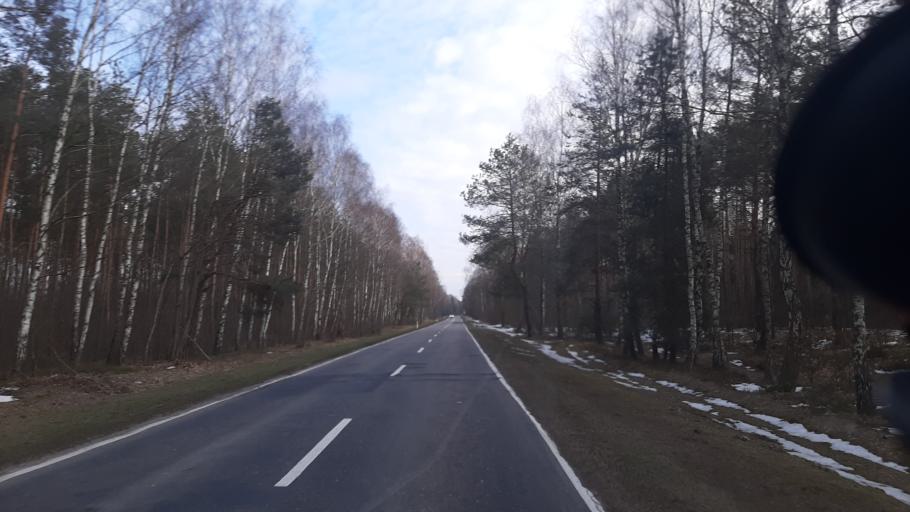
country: PL
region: Lublin Voivodeship
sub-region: Powiat lubartowski
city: Ostrow Lubelski
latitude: 51.4910
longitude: 22.8127
